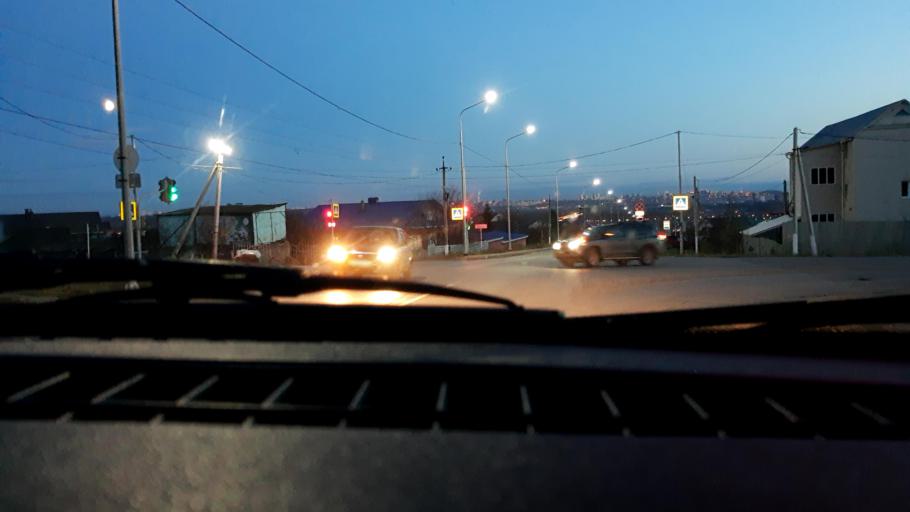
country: RU
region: Bashkortostan
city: Mikhaylovka
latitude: 54.8145
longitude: 55.8848
